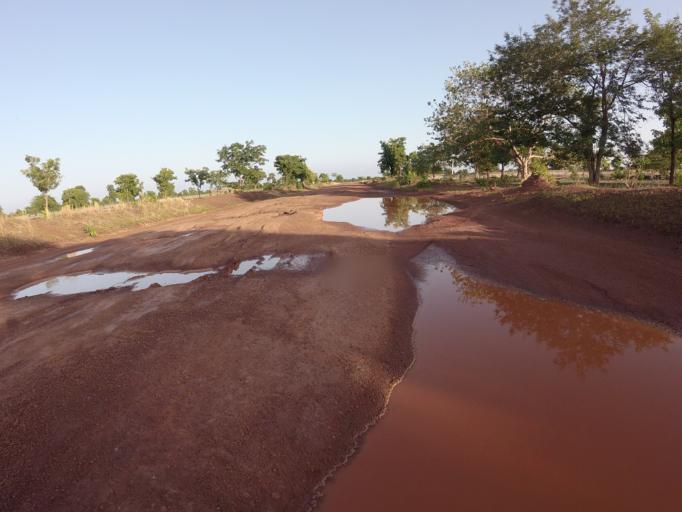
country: TG
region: Savanes
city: Sansanne-Mango
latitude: 10.2975
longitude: -0.0890
